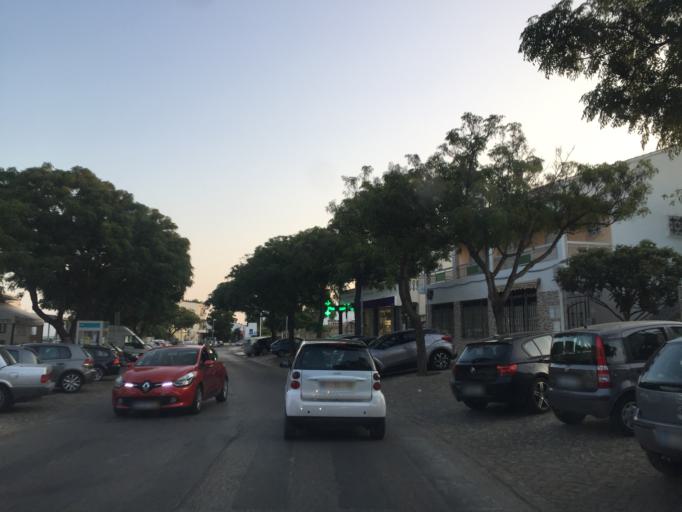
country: PT
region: Faro
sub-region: Loule
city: Almancil
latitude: 37.0911
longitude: -8.0278
